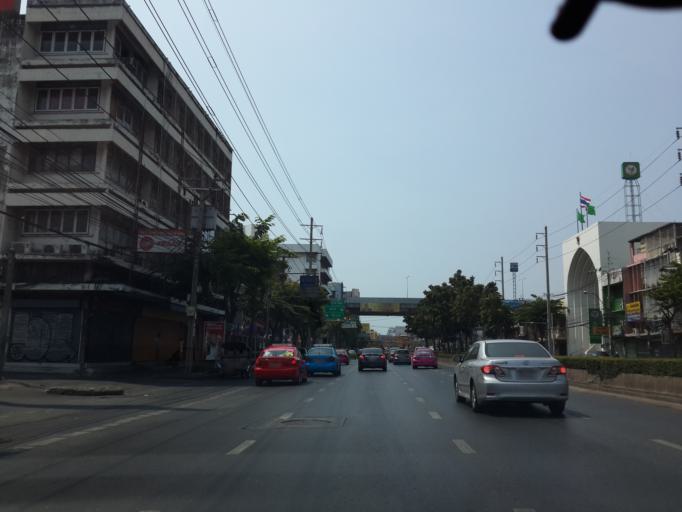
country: TH
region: Bangkok
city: Pathum Wan
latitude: 13.7362
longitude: 100.5204
